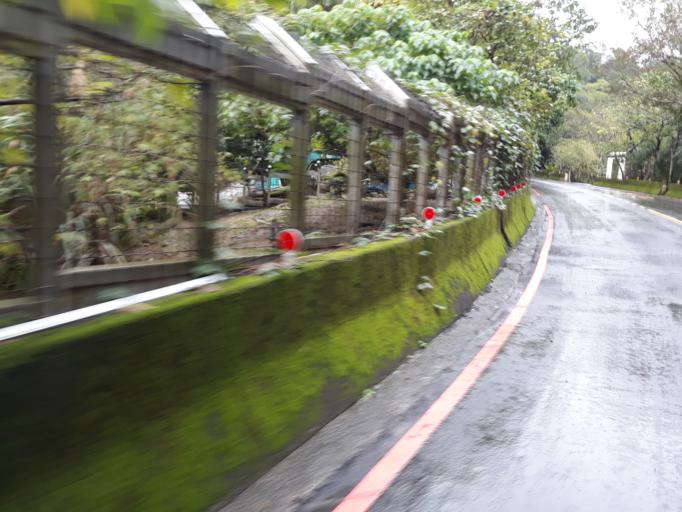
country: TW
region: Taipei
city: Taipei
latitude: 24.9935
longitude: 121.5901
